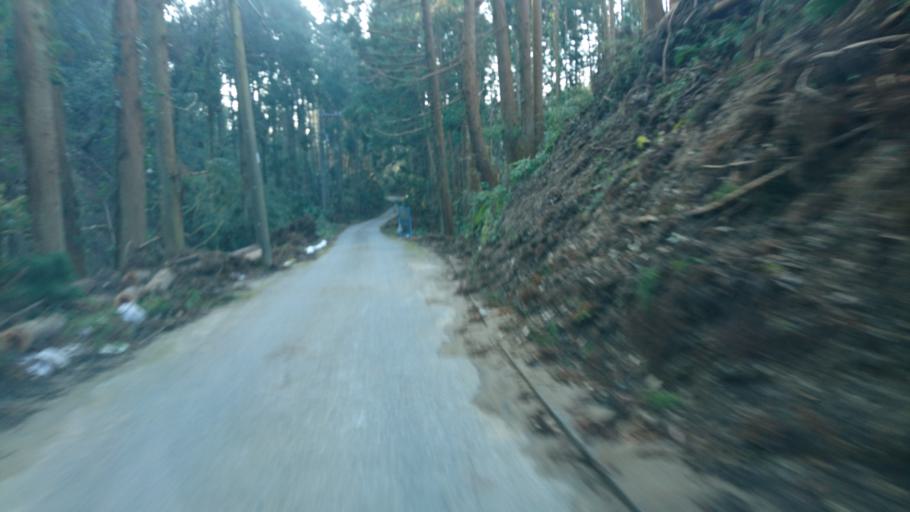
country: JP
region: Chiba
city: Kimitsu
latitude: 35.2881
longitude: 139.9547
